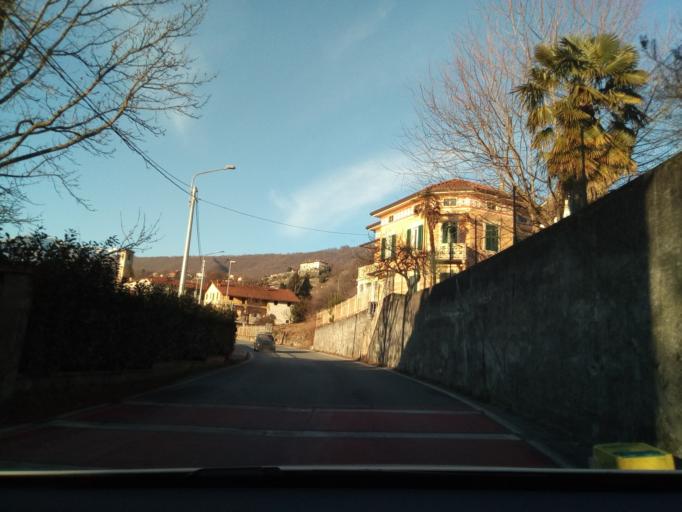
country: IT
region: Piedmont
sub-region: Provincia di Torino
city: Burolo
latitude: 45.4783
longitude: 7.9349
